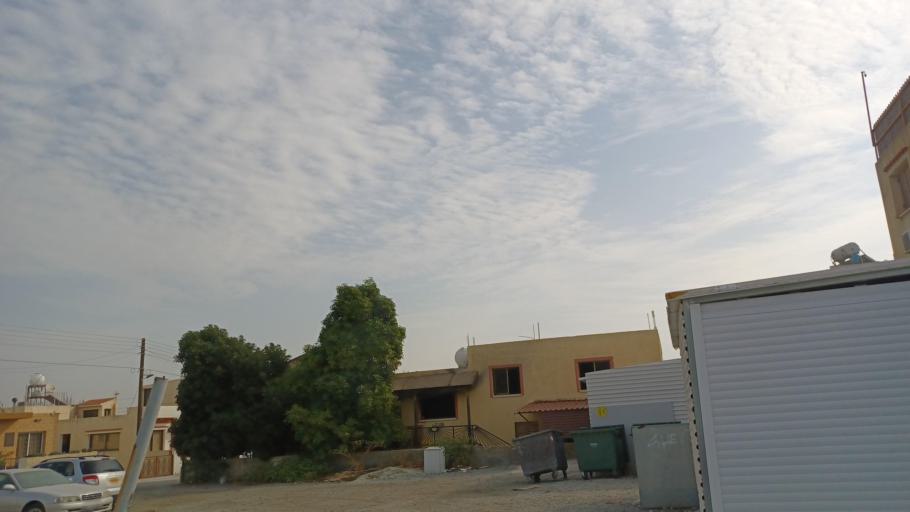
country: CY
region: Limassol
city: Ypsonas
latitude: 34.6956
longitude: 32.9453
